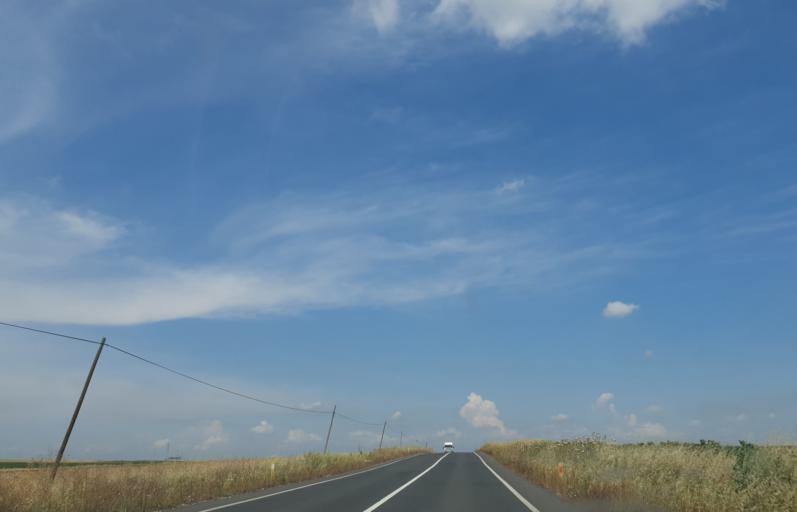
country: TR
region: Kirklareli
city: Buyukkaristiran
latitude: 41.2461
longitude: 27.6066
